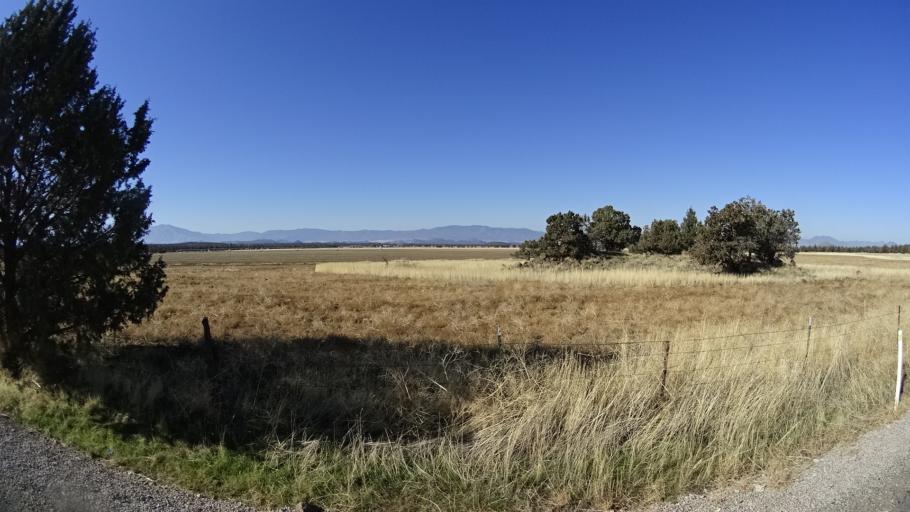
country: US
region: California
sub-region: Siskiyou County
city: Weed
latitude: 41.5985
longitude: -122.3020
